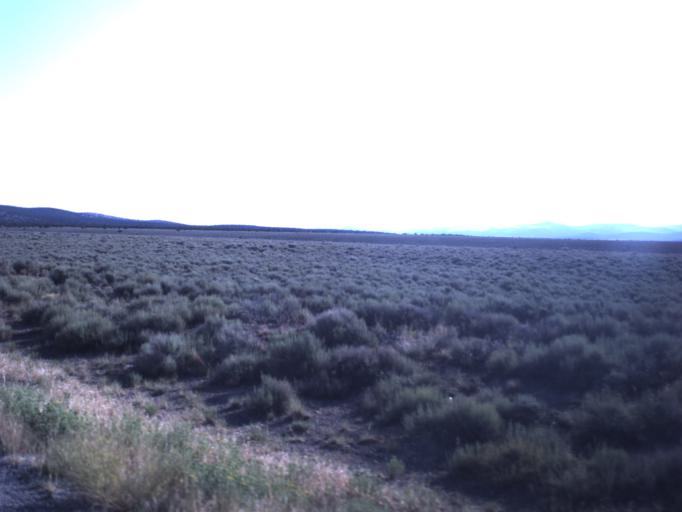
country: US
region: Utah
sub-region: Iron County
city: Enoch
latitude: 38.0025
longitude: -112.9978
